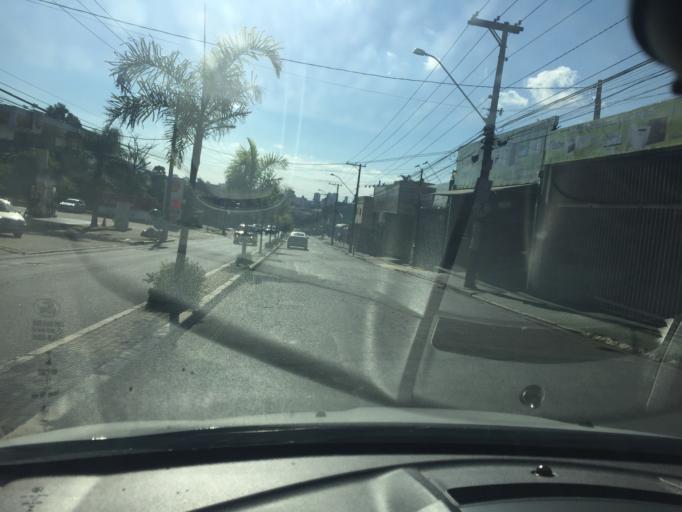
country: BR
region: Sao Paulo
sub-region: Varzea Paulista
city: Varzea Paulista
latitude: -23.2080
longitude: -46.8501
